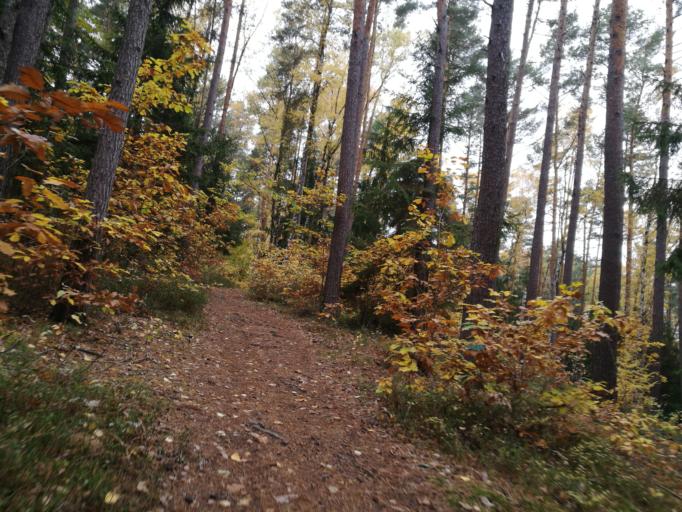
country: DE
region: Bavaria
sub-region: Regierungsbezirk Mittelfranken
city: Zirndorf
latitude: 49.4687
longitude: 10.9329
